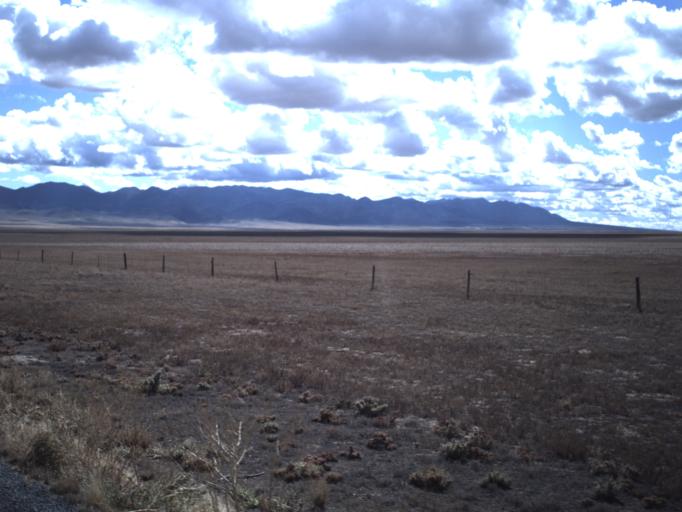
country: US
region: Utah
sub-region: Beaver County
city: Milford
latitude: 38.5520
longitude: -113.7353
